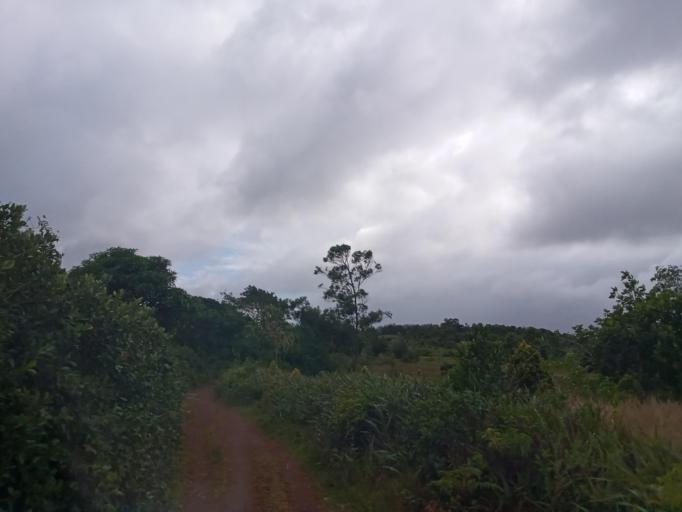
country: MG
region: Atsimo-Atsinanana
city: Vohipaho
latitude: -23.7761
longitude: 47.5361
